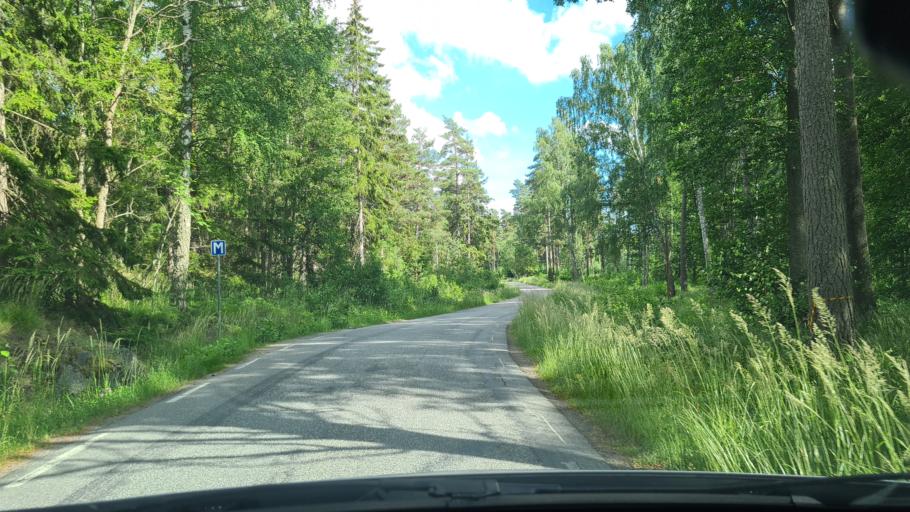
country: SE
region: Stockholm
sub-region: Vaxholms Kommun
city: Vaxholm
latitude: 59.4119
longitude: 18.4470
